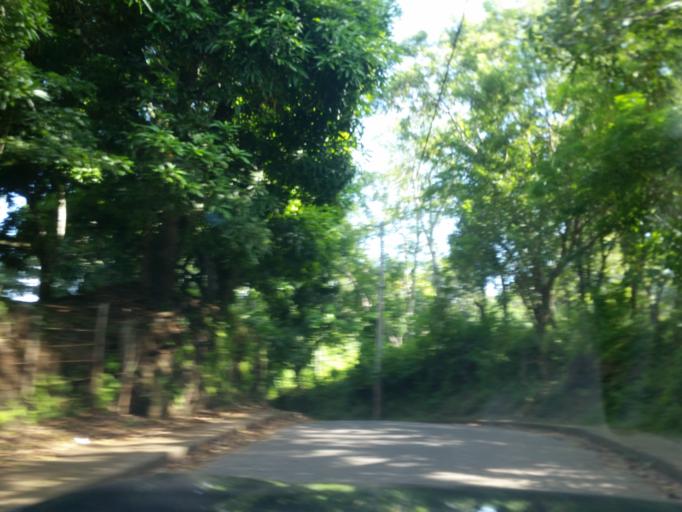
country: NI
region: Masaya
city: Catarina
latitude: 11.9341
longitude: -86.0666
